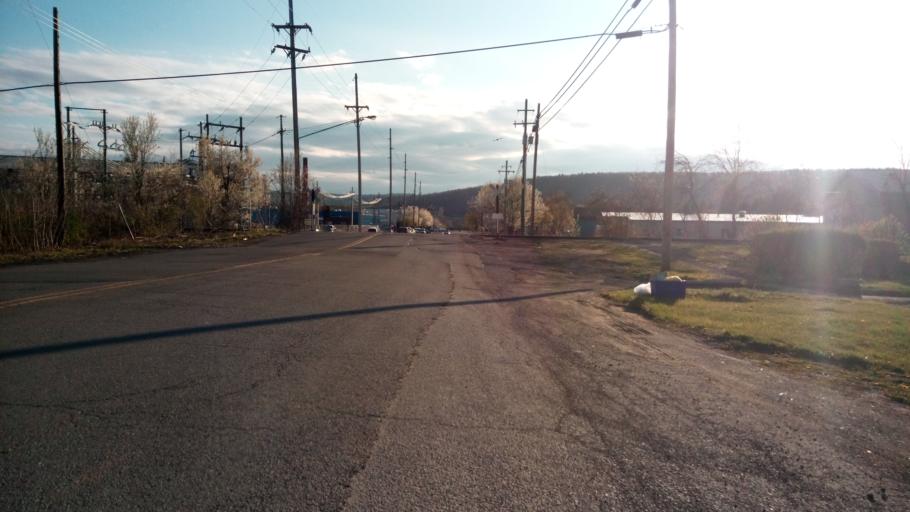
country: US
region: New York
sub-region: Chemung County
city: Elmira Heights
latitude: 42.1217
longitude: -76.8164
